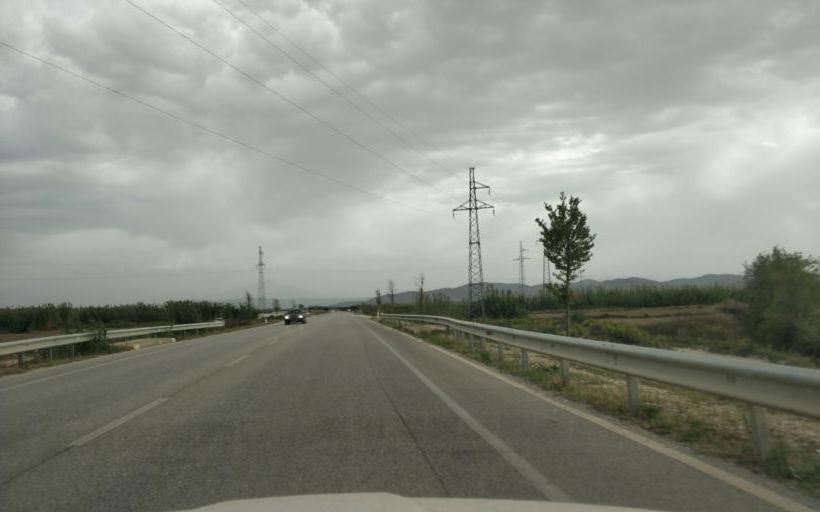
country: AL
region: Fier
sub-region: Rrethi i Fierit
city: Frakulla e Madhe
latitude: 40.6410
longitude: 19.5012
